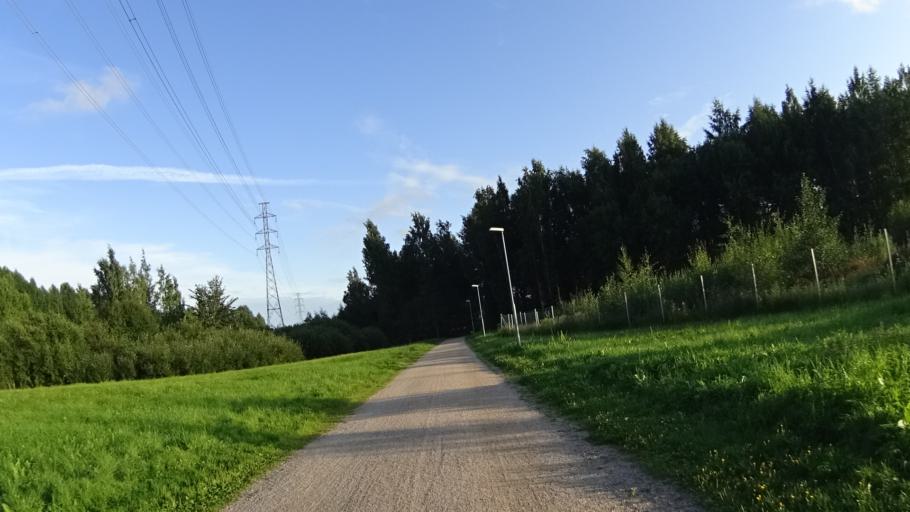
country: FI
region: Uusimaa
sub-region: Helsinki
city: Teekkarikylae
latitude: 60.2365
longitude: 24.8660
